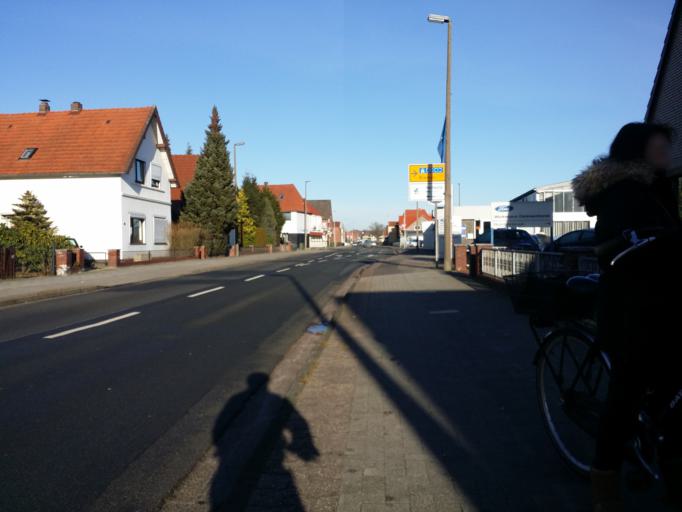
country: DE
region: Lower Saxony
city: Delmenhorst
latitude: 53.0481
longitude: 8.6574
